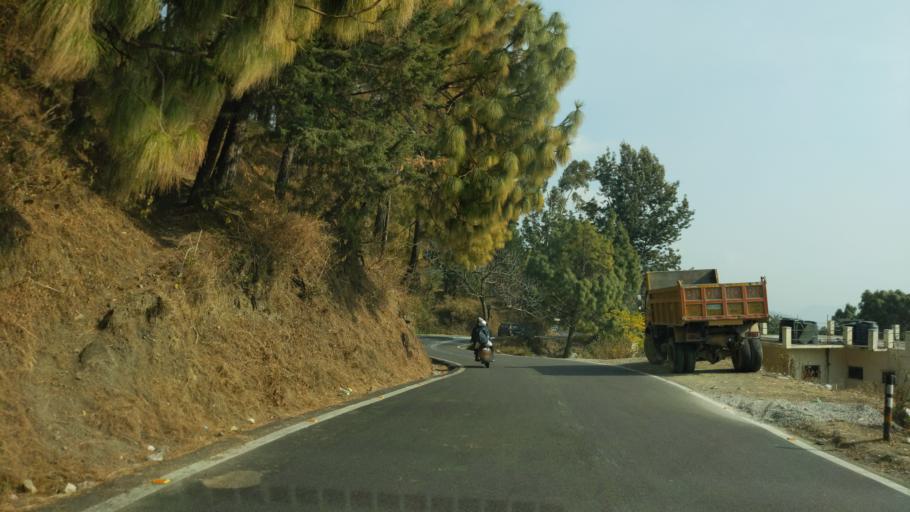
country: IN
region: Uttarakhand
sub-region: Naini Tal
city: Bhowali
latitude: 29.3782
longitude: 79.5309
